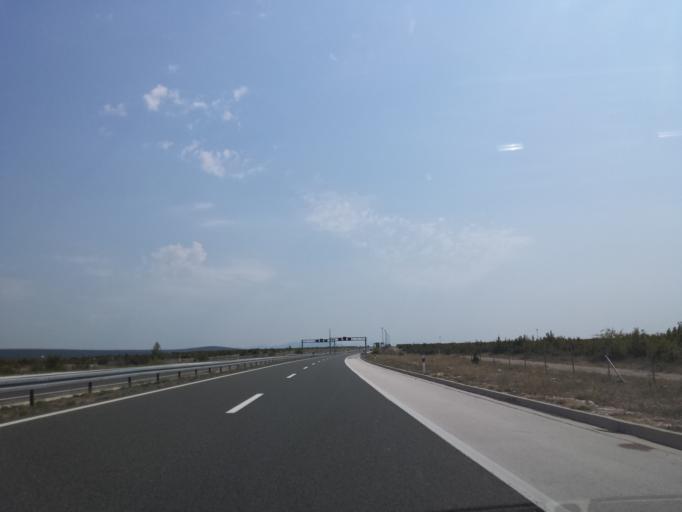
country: HR
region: Sibensko-Kniniska
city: Zaton
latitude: 43.8969
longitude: 15.7811
